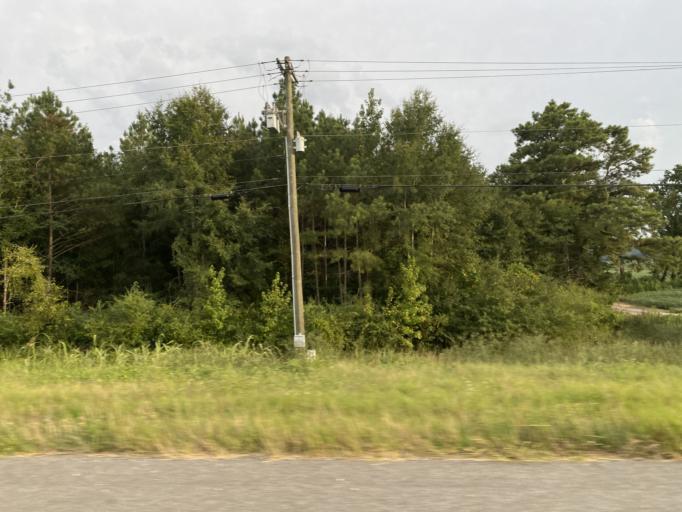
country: US
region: Alabama
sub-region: Franklin County
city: Red Bay
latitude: 34.4492
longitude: -88.0749
